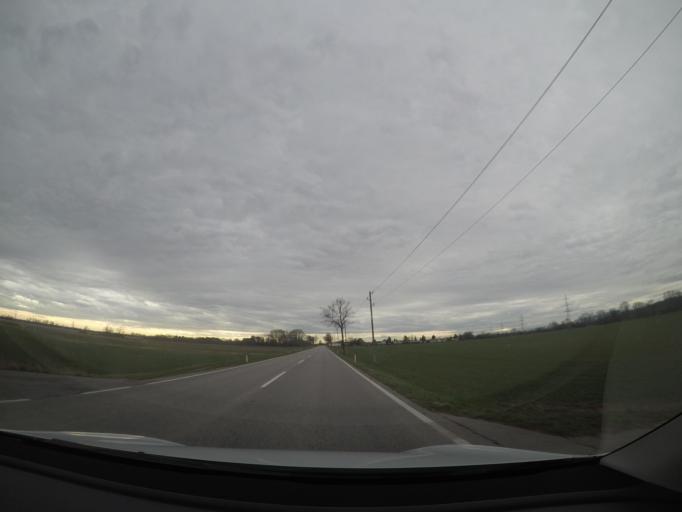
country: AT
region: Lower Austria
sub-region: Politischer Bezirk Modling
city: Achau
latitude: 48.0642
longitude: 16.3820
